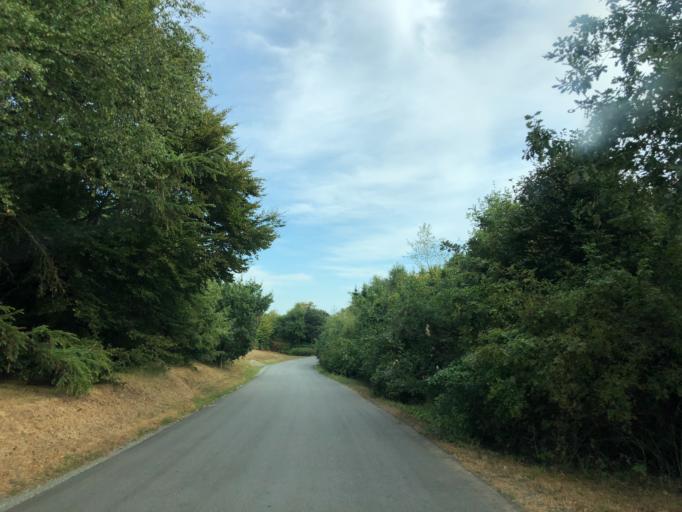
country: DK
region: South Denmark
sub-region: Vejle Kommune
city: Egtved
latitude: 55.6813
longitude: 9.2662
